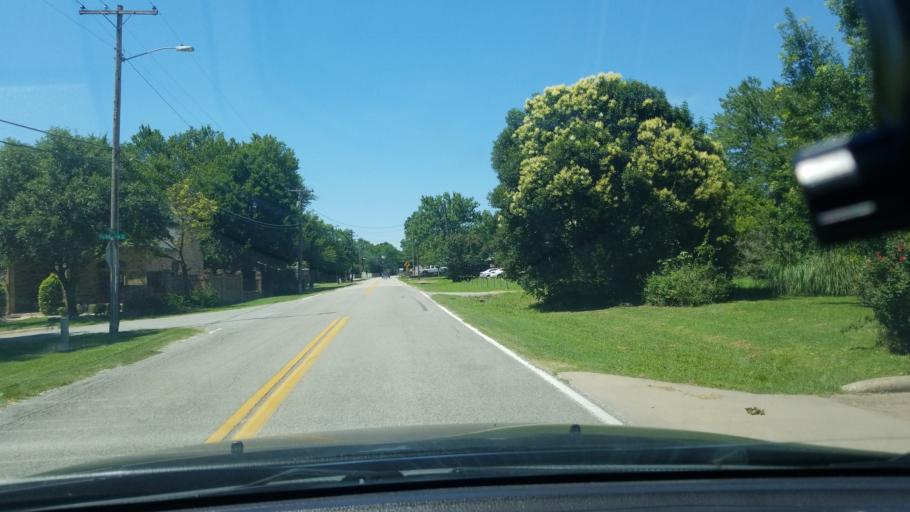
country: US
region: Texas
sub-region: Dallas County
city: Mesquite
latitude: 32.7595
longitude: -96.6052
